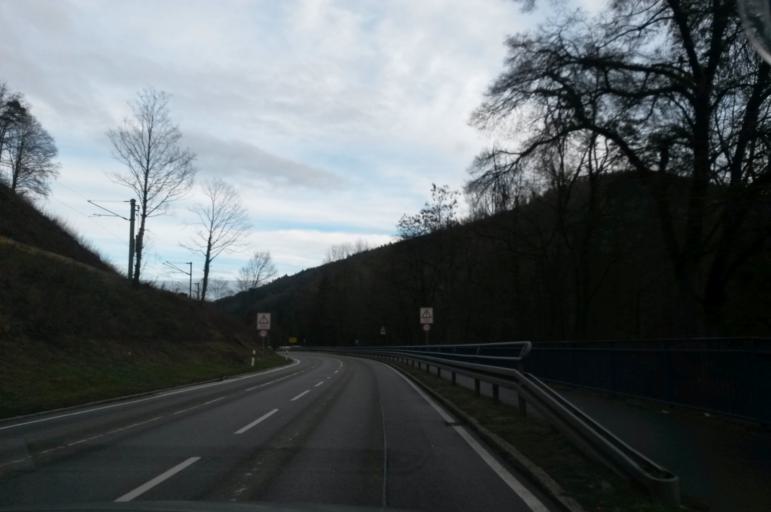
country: DE
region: Baden-Wuerttemberg
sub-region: Karlsruhe Region
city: Neuenburg
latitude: 48.8544
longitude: 8.6125
